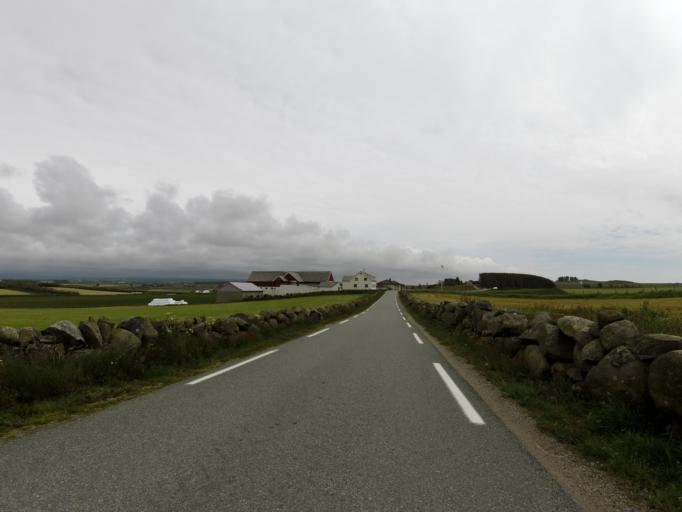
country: NO
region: Rogaland
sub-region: Ha
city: Naerbo
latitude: 58.6650
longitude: 5.5536
